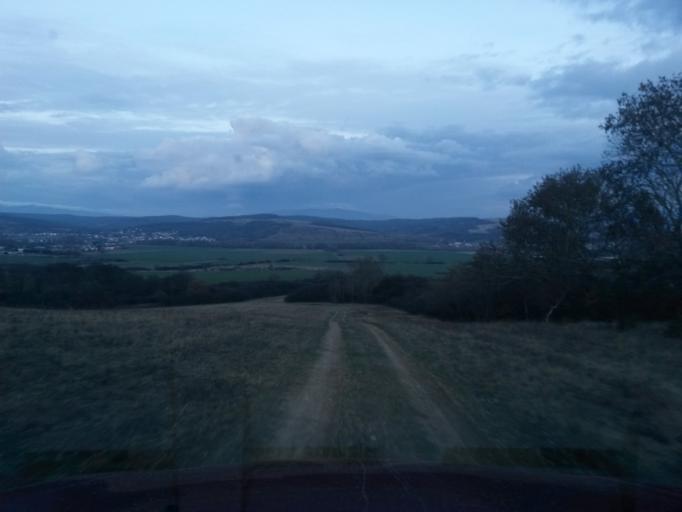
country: SK
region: Kosicky
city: Kosice
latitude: 48.6999
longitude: 21.3157
